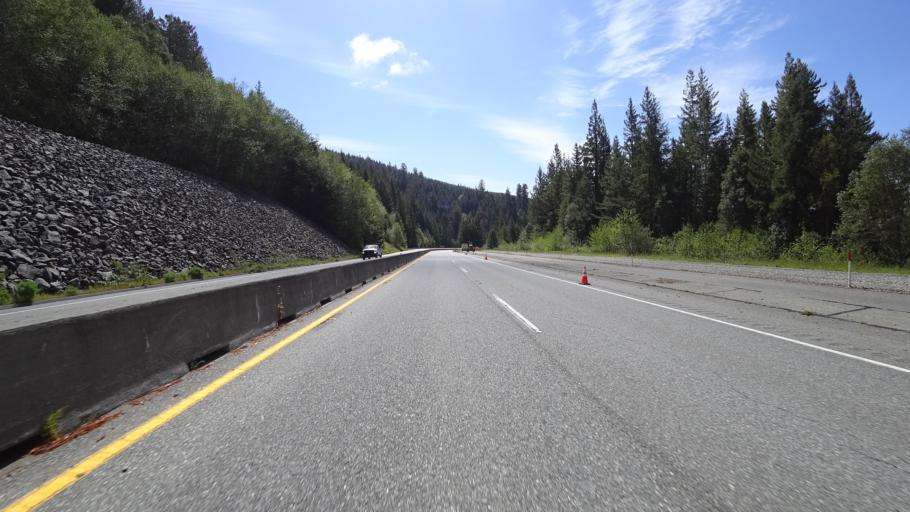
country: US
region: California
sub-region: Humboldt County
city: Westhaven-Moonstone
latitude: 41.3742
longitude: -123.9928
